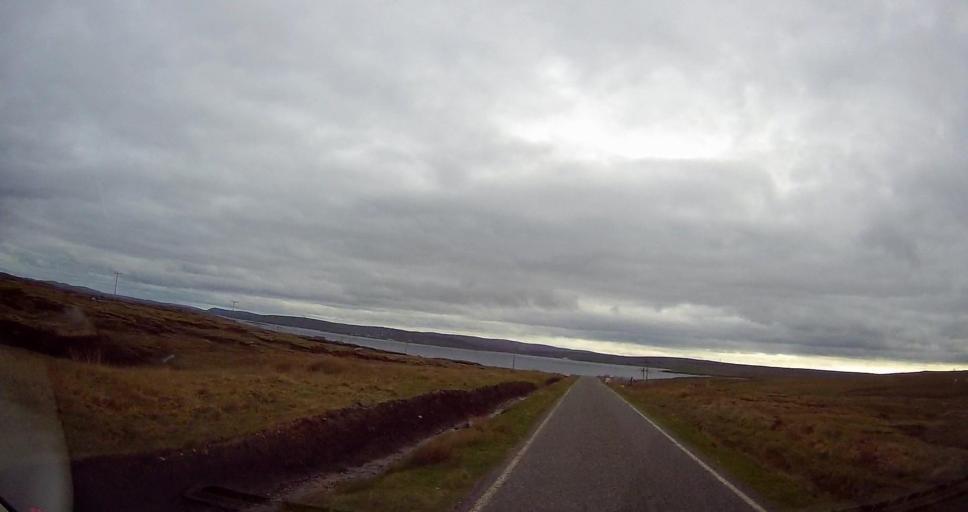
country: GB
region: Scotland
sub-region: Shetland Islands
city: Shetland
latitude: 60.5018
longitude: -1.1499
